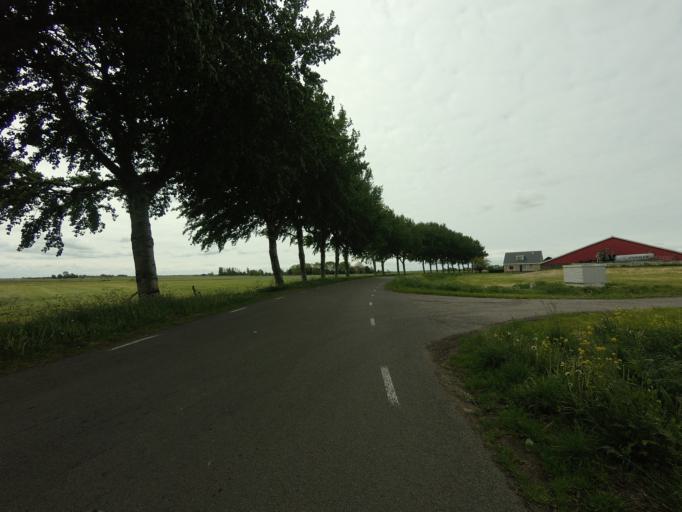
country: NL
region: Friesland
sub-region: Sudwest Fryslan
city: Workum
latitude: 52.9488
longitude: 5.4984
